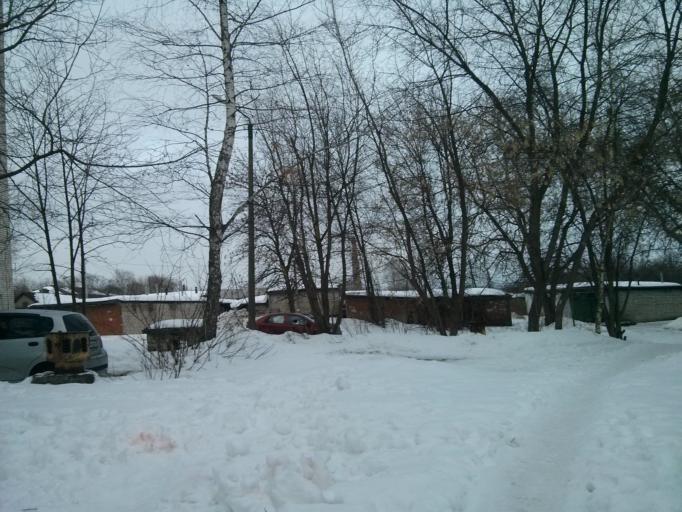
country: RU
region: Vladimir
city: Murom
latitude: 55.5536
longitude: 42.0560
